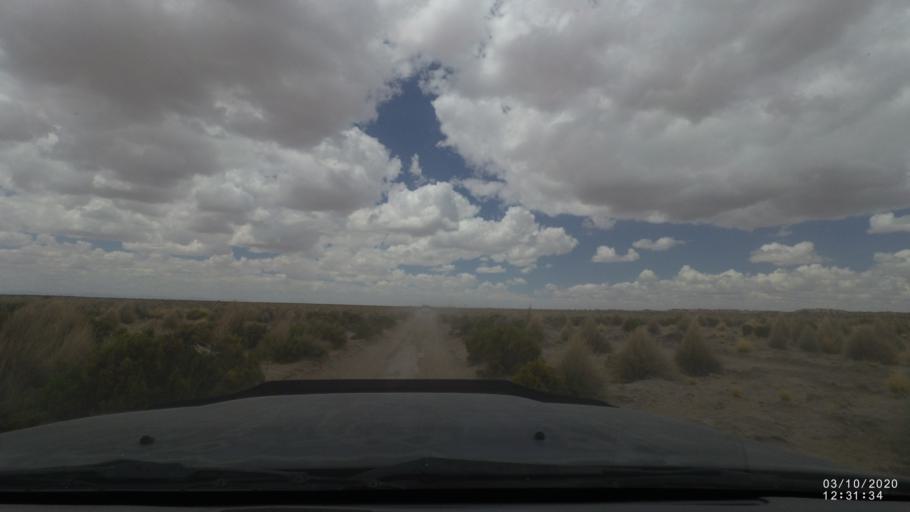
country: BO
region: Oruro
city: Poopo
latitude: -18.6866
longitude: -67.5384
